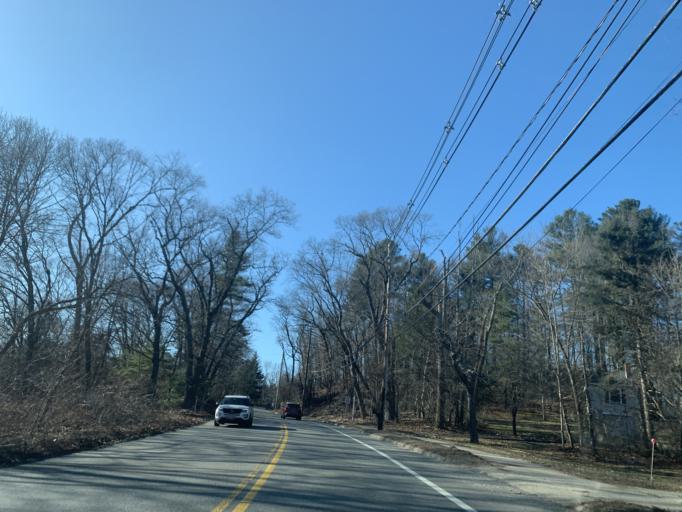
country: US
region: Massachusetts
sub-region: Middlesex County
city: Sudbury
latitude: 42.3617
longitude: -71.4059
